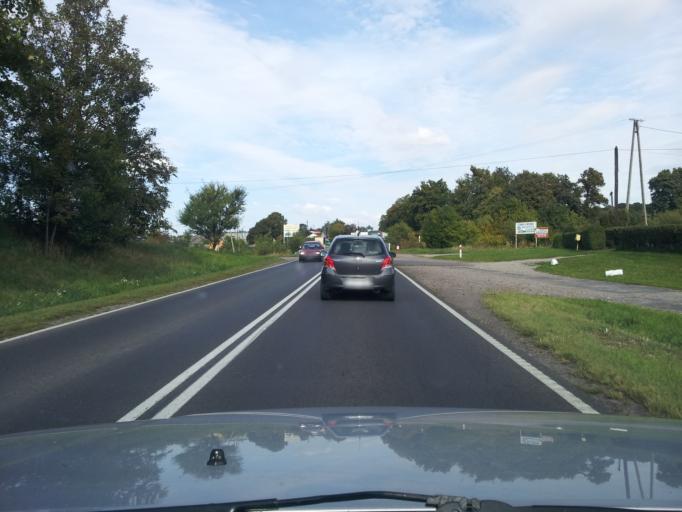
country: PL
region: Kujawsko-Pomorskie
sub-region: Powiat brodnicki
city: Brzozie
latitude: 53.2946
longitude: 19.5010
